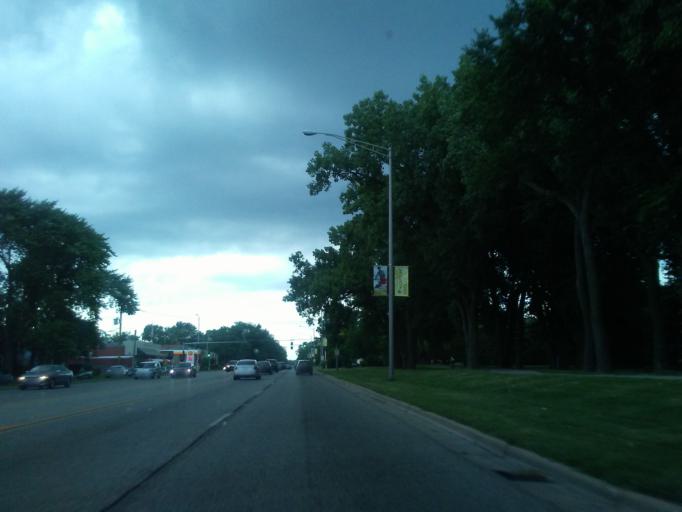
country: US
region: Illinois
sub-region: Cook County
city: Skokie
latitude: 42.0323
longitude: -87.7109
